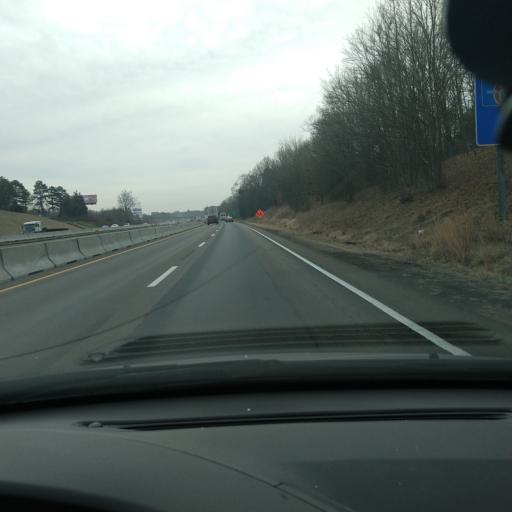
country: US
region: North Carolina
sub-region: Rowan County
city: Landis
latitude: 35.5147
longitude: -80.5686
